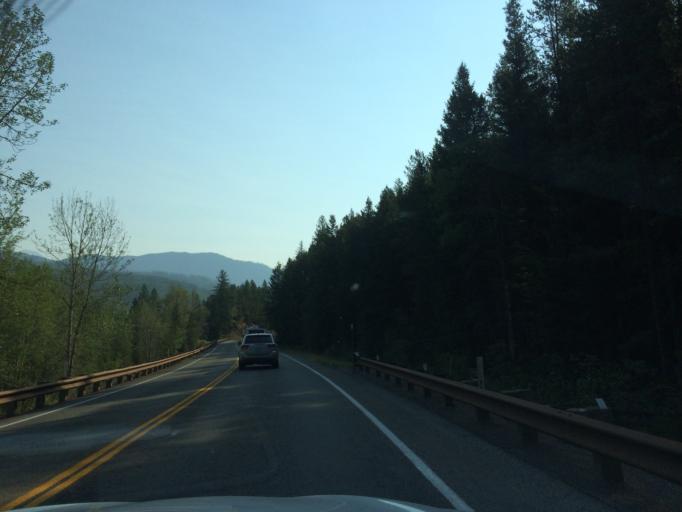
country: US
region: Montana
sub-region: Flathead County
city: Columbia Falls
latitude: 48.4902
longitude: -113.8672
